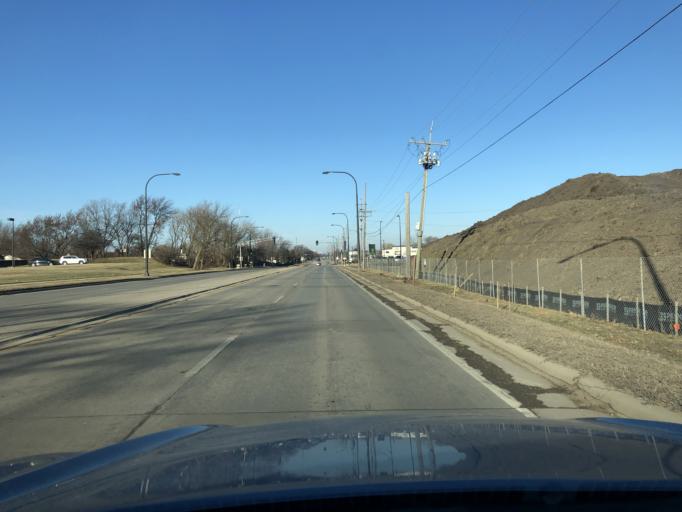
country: US
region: Illinois
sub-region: DuPage County
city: Itasca
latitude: 41.9914
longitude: -88.0312
